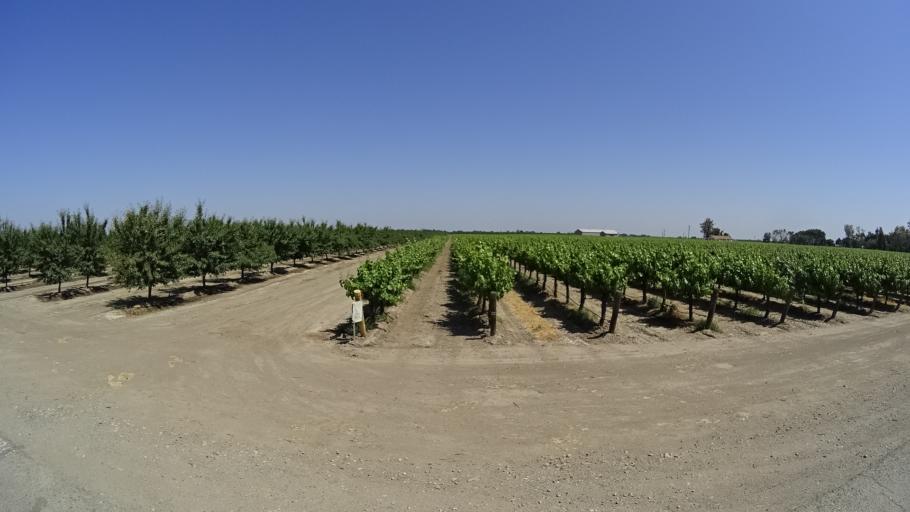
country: US
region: California
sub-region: Kings County
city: Lemoore
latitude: 36.3718
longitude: -119.7670
